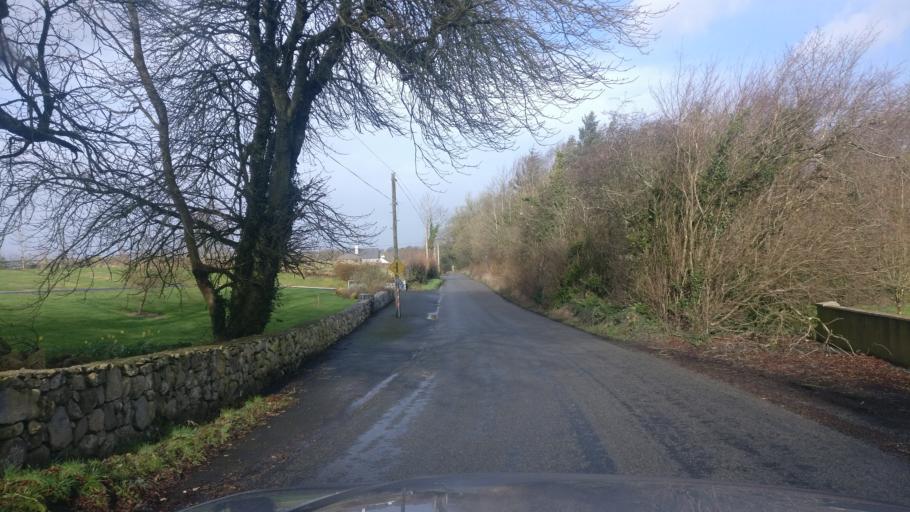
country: IE
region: Connaught
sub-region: County Galway
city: Loughrea
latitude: 53.2784
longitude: -8.5821
